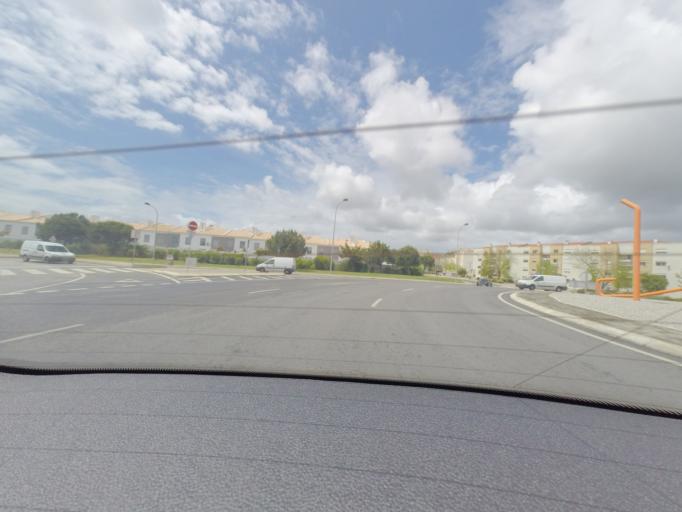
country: PT
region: Lisbon
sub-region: Cascais
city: Alcabideche
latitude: 38.7348
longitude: -9.3882
